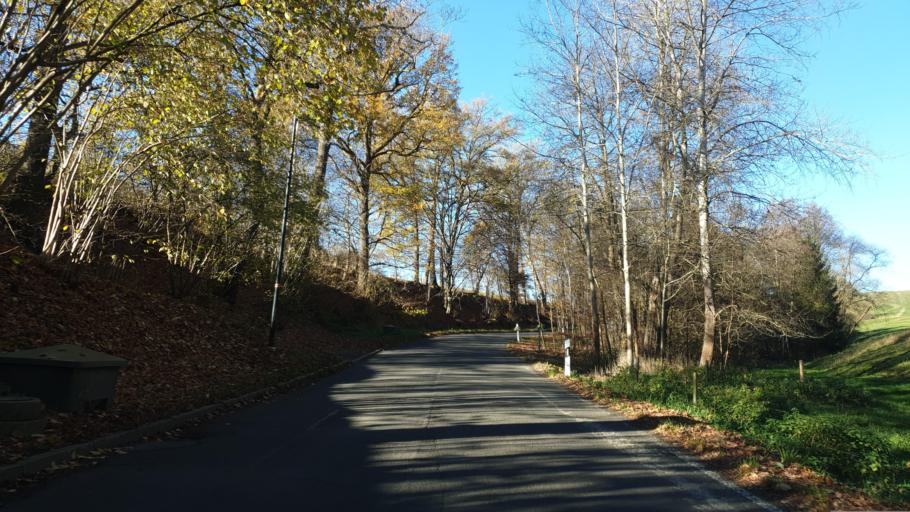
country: DE
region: Saxony
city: Elsterberg
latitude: 50.6059
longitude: 12.1441
